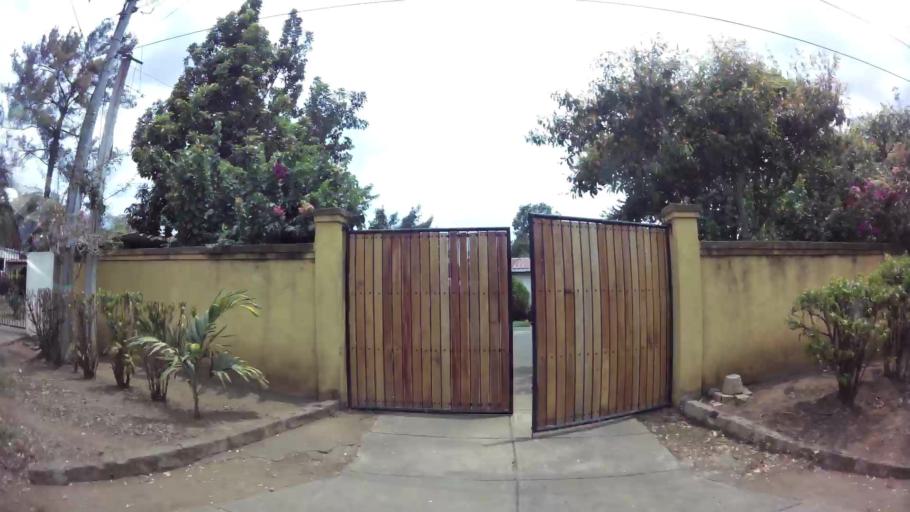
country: NI
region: Managua
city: Managua
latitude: 12.0951
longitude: -86.2285
